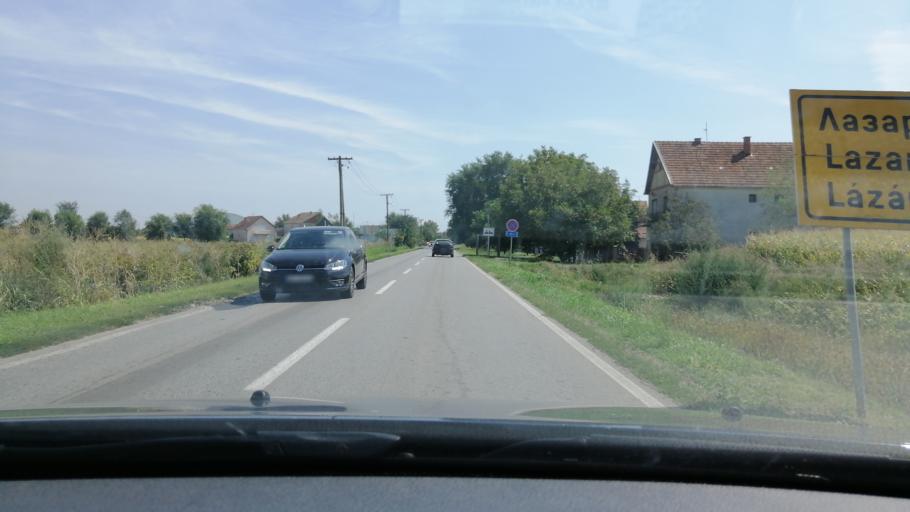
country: RS
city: Lazarevo
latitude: 45.3880
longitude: 20.5234
